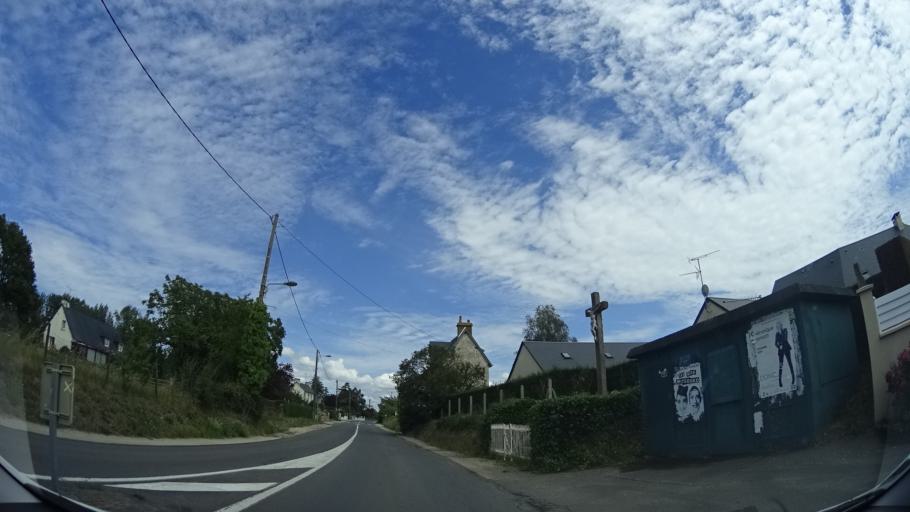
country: FR
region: Lower Normandy
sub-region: Departement de la Manche
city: Sartilly
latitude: 48.6843
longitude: -1.4718
